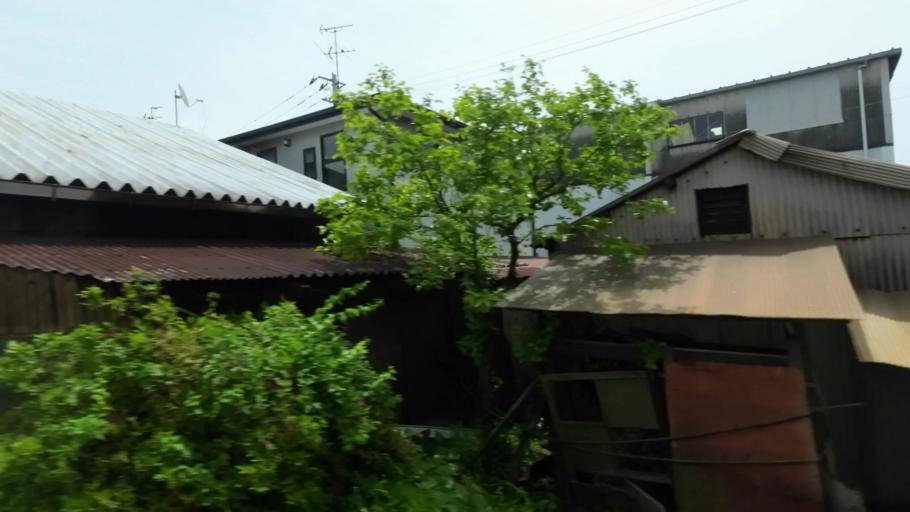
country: JP
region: Kochi
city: Kochi-shi
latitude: 33.6032
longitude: 133.6757
